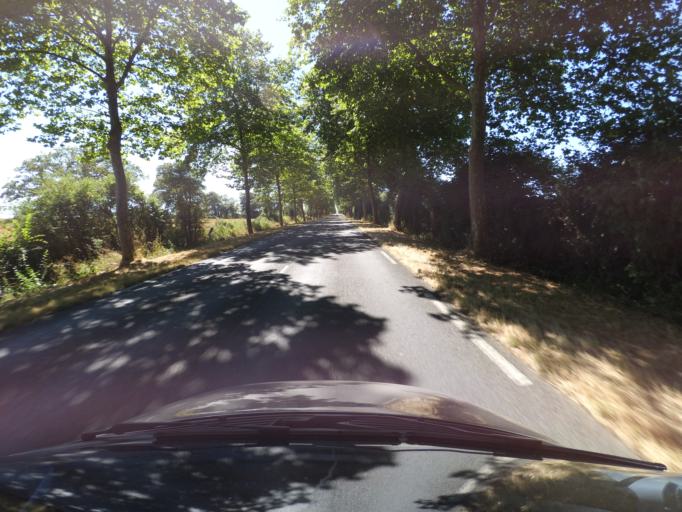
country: FR
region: Pays de la Loire
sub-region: Departement de Maine-et-Loire
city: La Tourlandry
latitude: 47.1231
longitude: -0.6826
